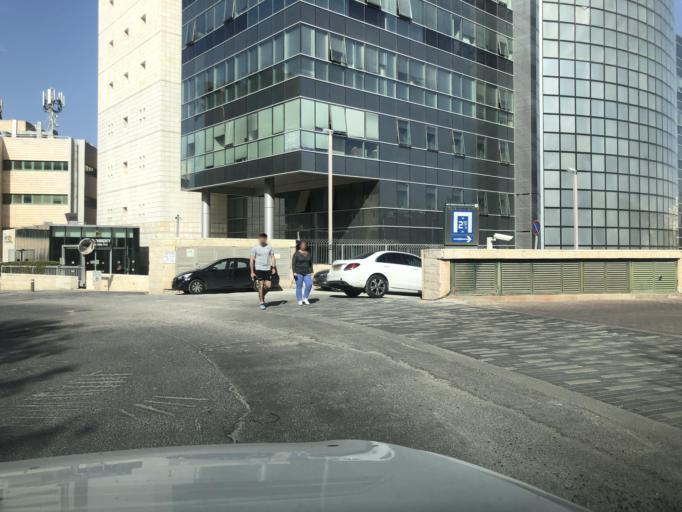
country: IL
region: Jerusalem
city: West Jerusalem
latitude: 31.8034
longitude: 35.2132
